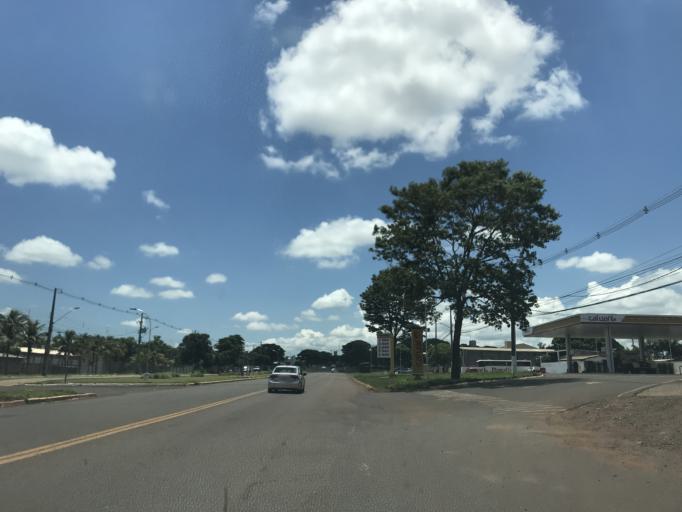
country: BR
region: Parana
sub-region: Marialva
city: Marialva
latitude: -23.4763
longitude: -51.8112
